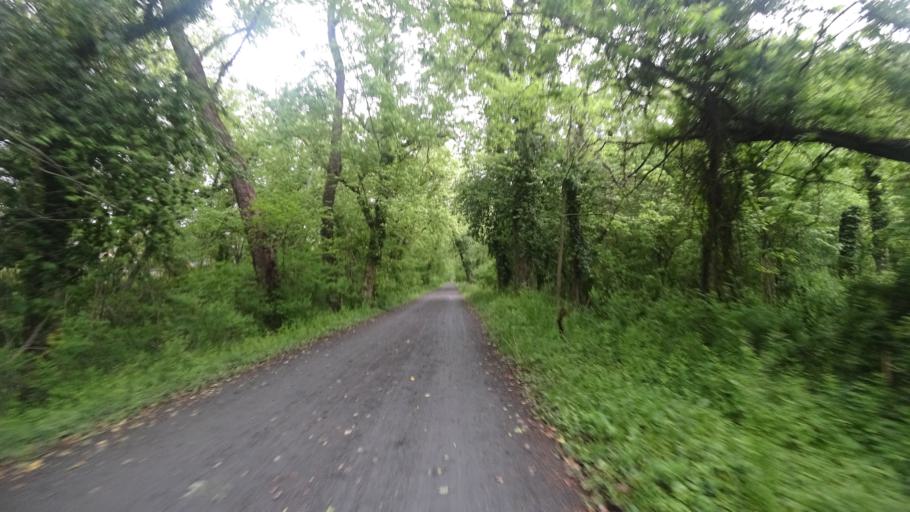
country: US
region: Maryland
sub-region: Frederick County
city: Brunswick
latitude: 39.3138
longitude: -77.6405
